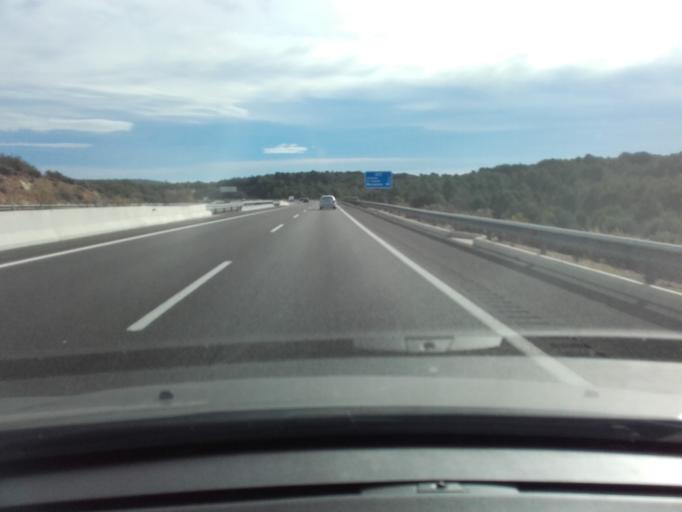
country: ES
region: Catalonia
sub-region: Provincia de Tarragona
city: el Catllar
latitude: 41.1411
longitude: 1.3248
